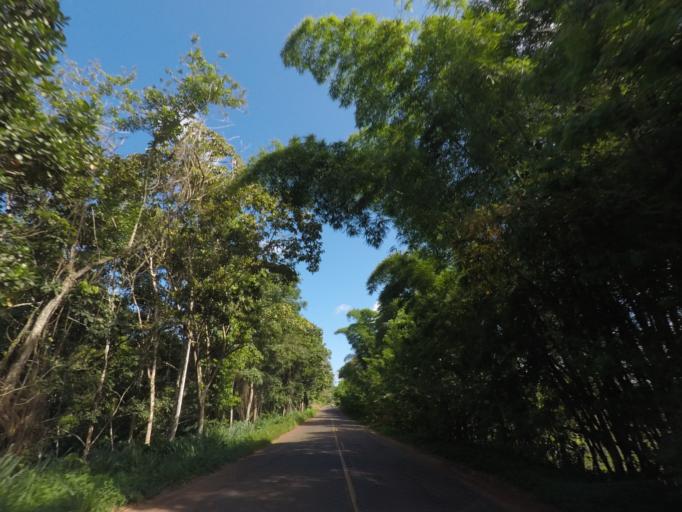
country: BR
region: Bahia
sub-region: Camamu
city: Camamu
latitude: -13.9123
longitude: -39.1293
